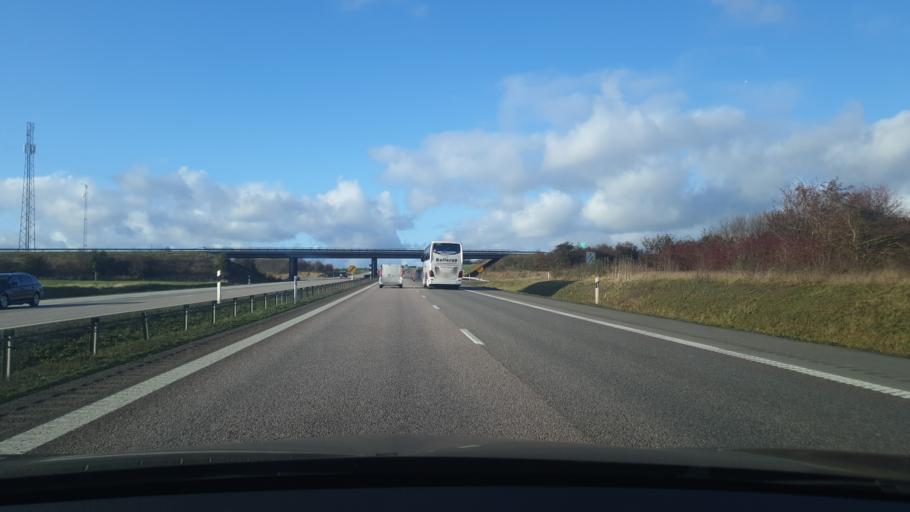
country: SE
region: Skane
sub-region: Helsingborg
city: Glumslov
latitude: 55.9233
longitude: 12.8386
